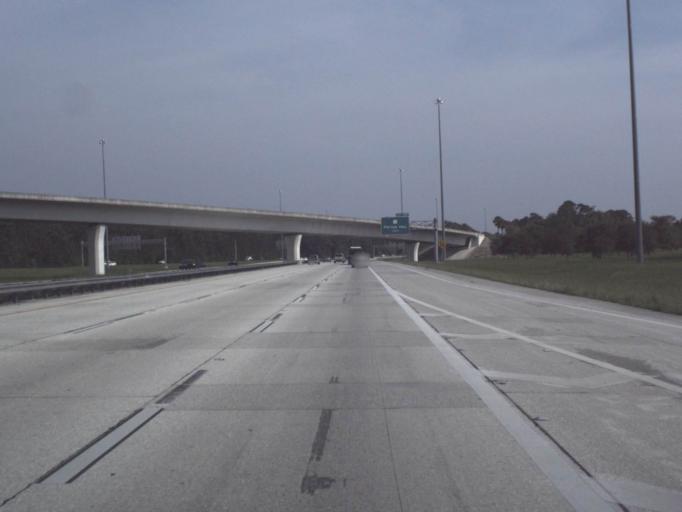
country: US
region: Florida
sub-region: Saint Johns County
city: Fruit Cove
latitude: 30.1690
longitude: -81.5559
